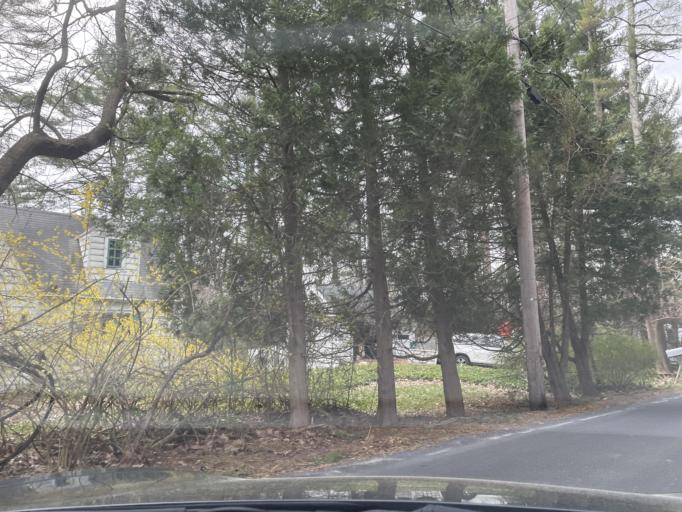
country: US
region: New York
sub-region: Ulster County
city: Woodstock
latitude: 42.0380
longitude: -74.1082
